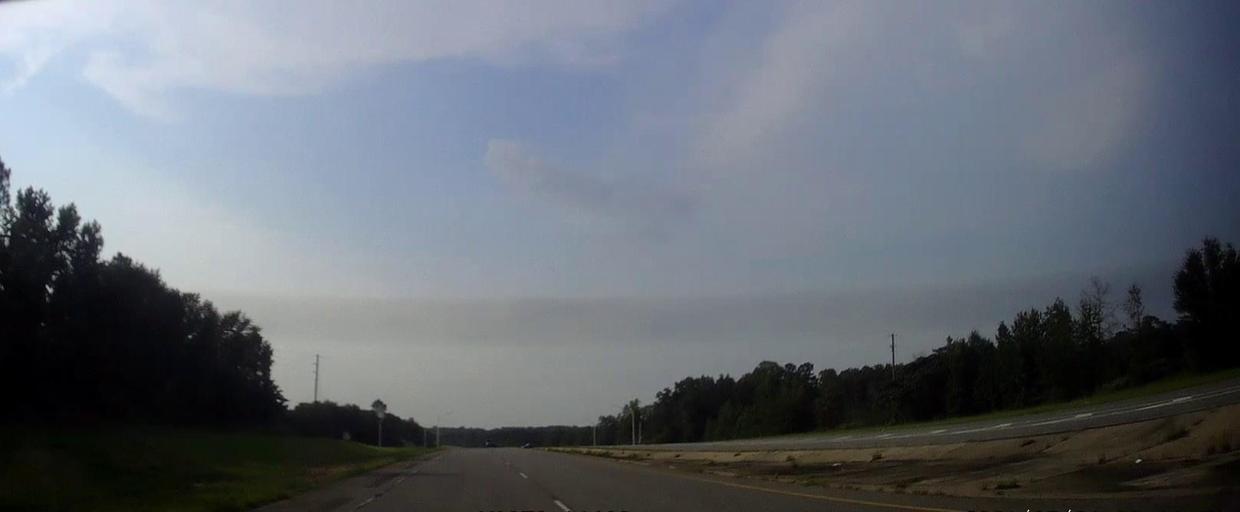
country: US
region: Georgia
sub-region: Laurens County
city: Dublin
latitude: 32.5332
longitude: -82.9689
